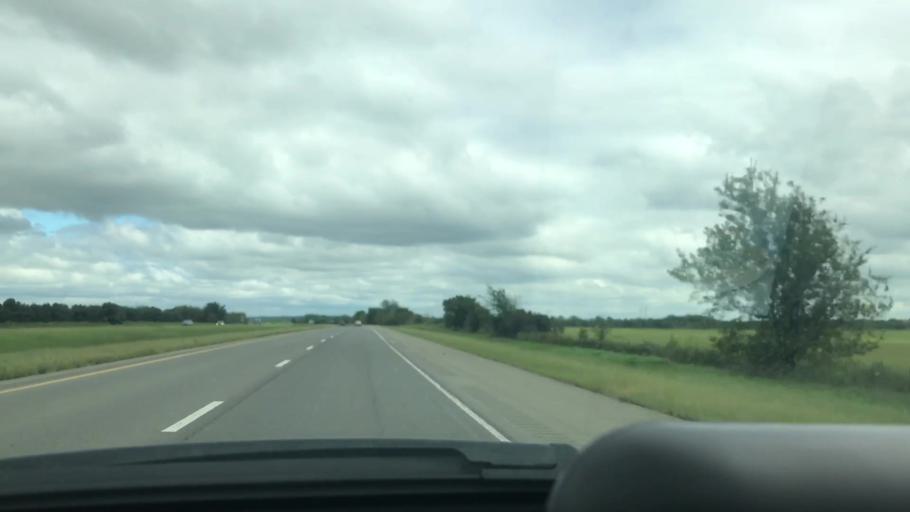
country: US
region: Oklahoma
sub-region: McIntosh County
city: Checotah
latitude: 35.5977
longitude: -95.4821
